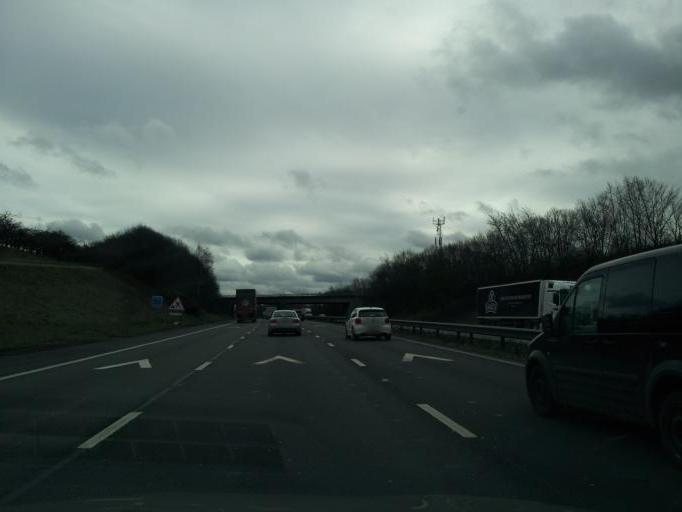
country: GB
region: England
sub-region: Staffordshire
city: Barlaston
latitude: 52.9263
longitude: -2.2088
